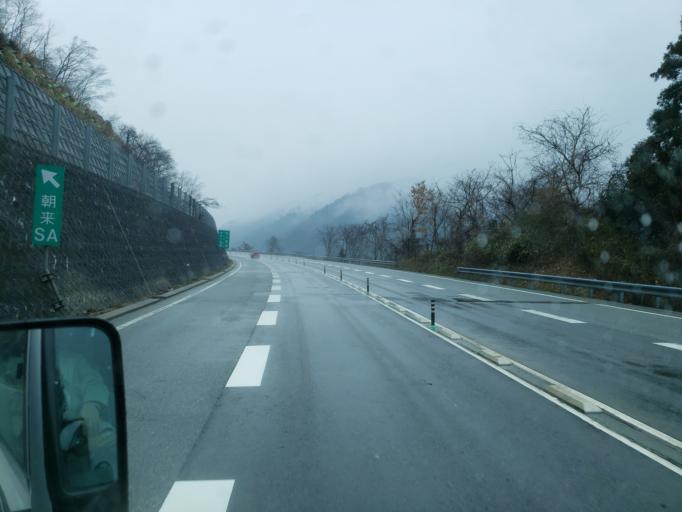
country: JP
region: Hyogo
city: Nishiwaki
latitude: 35.2078
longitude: 134.7939
